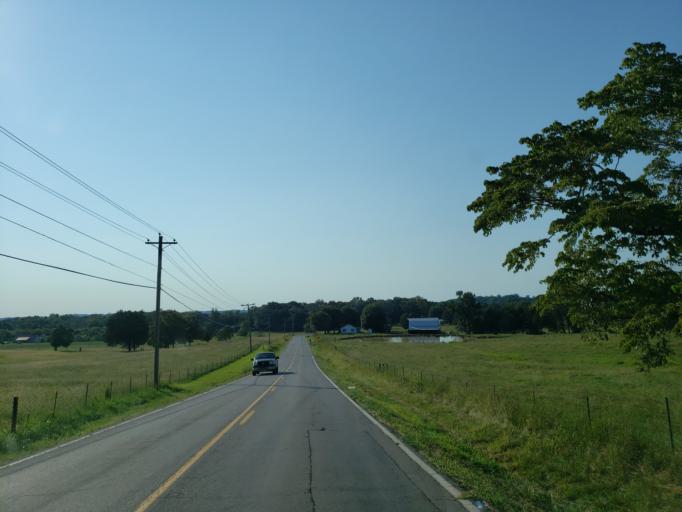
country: US
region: Tennessee
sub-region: Bradley County
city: Wildwood Lake
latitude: 35.0958
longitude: -84.8043
